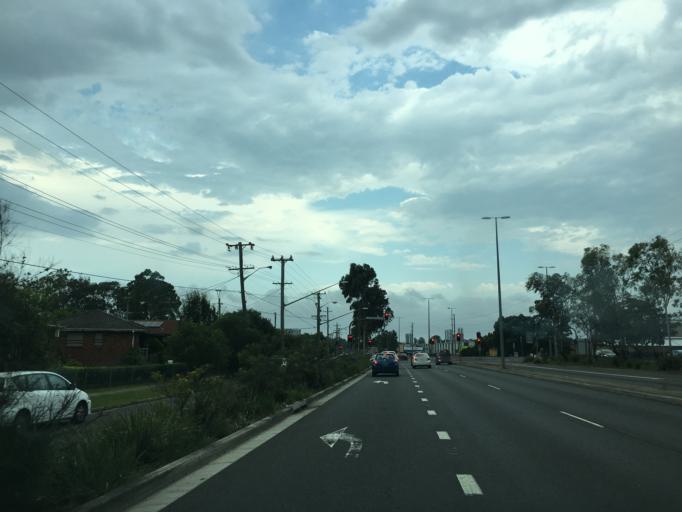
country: AU
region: New South Wales
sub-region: Liverpool
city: Miller
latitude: -33.9274
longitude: 150.8893
